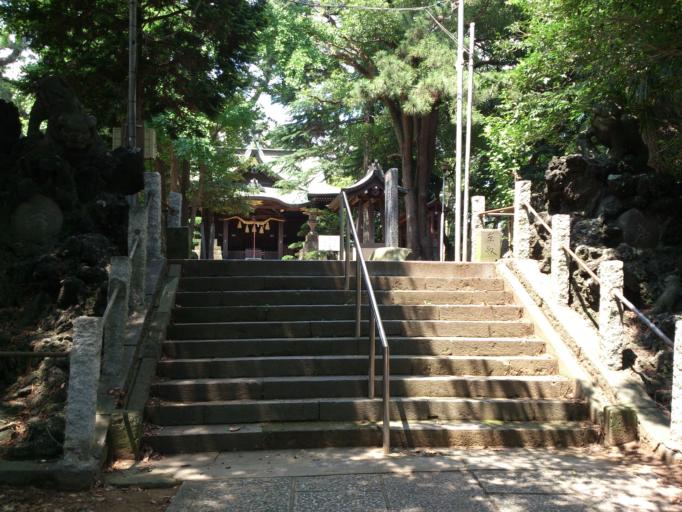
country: JP
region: Chiba
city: Funabashi
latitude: 35.7075
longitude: 139.9673
